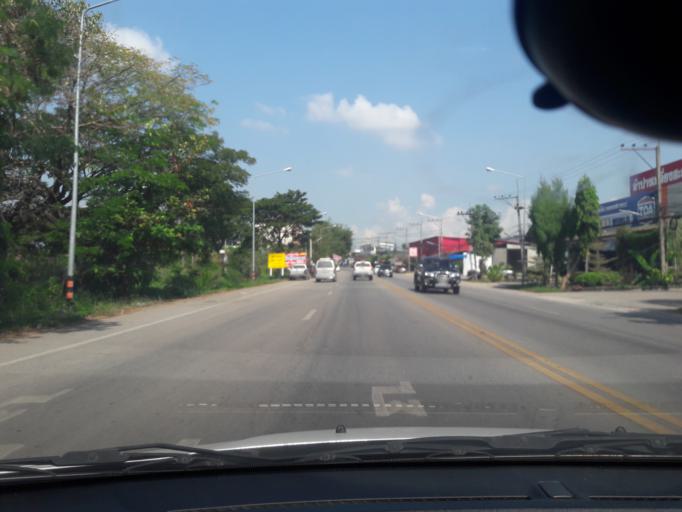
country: TH
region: Lampang
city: Lampang
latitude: 18.2467
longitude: 99.4909
